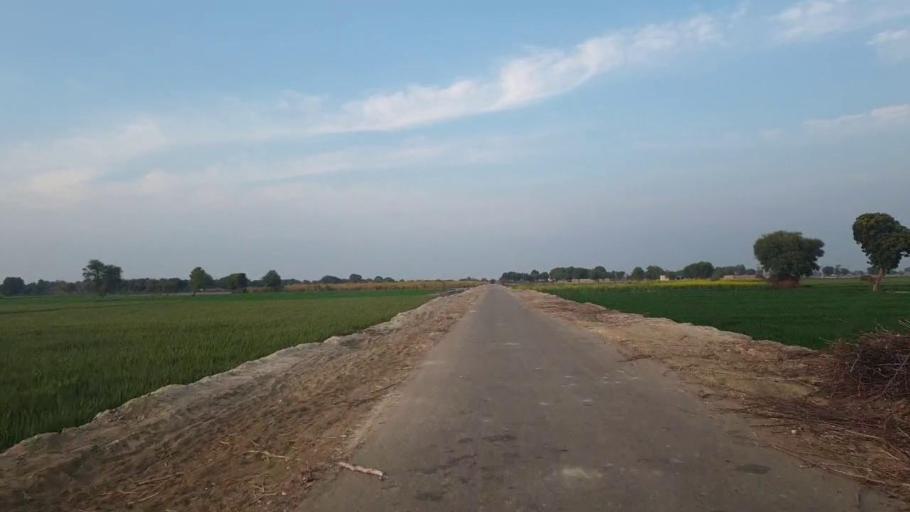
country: PK
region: Sindh
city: Shahpur Chakar
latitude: 26.1054
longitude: 68.5465
